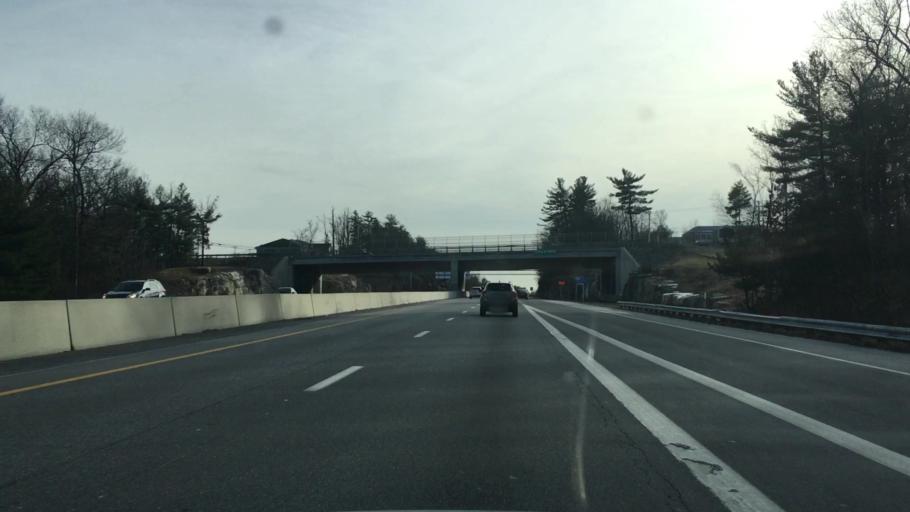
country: US
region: New Hampshire
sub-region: Hillsborough County
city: Bedford
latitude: 42.9440
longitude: -71.4708
